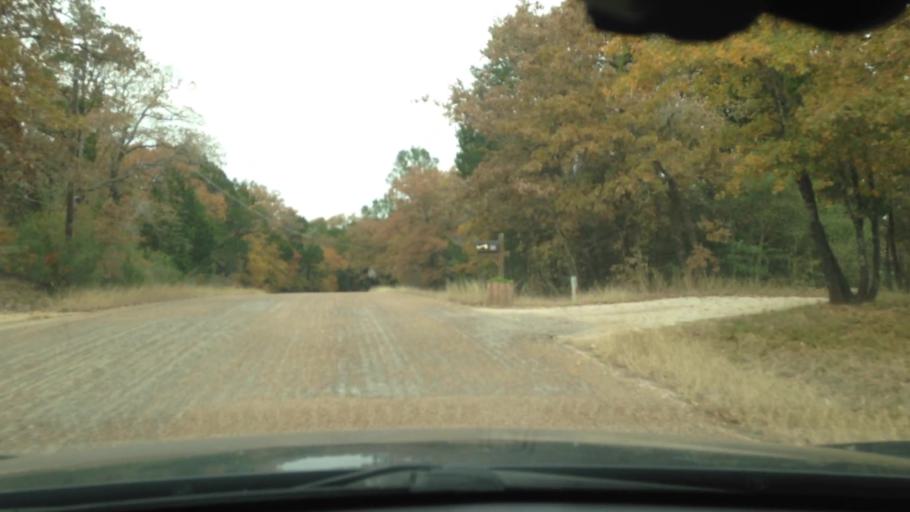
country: US
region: Texas
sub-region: Bastrop County
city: Bastrop
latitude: 30.1335
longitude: -97.2852
